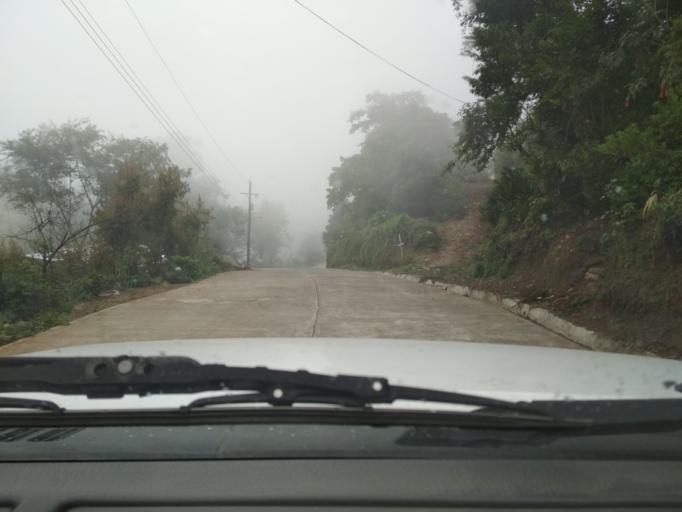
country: MX
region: Veracruz
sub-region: La Perla
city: Barrio de San Miguel
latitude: 18.9520
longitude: -97.1237
